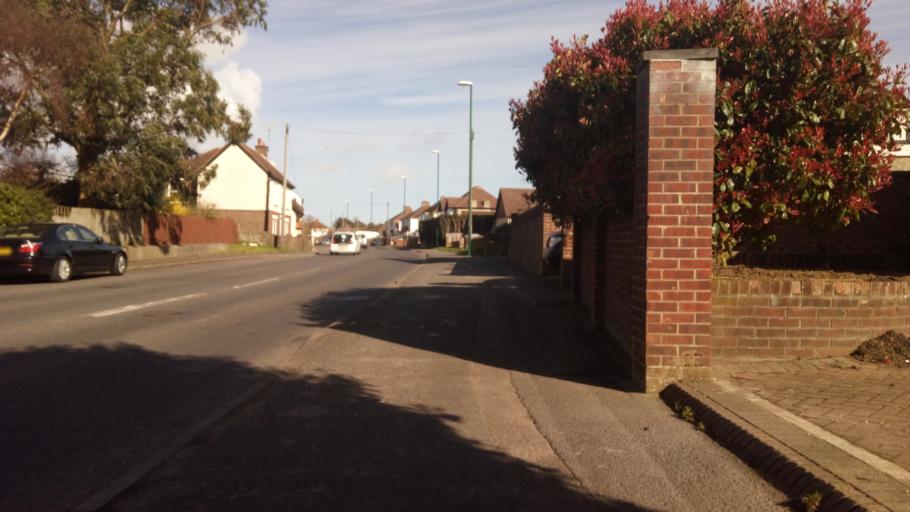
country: GB
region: England
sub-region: West Sussex
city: Bognor Regis
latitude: 50.7922
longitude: -0.6495
